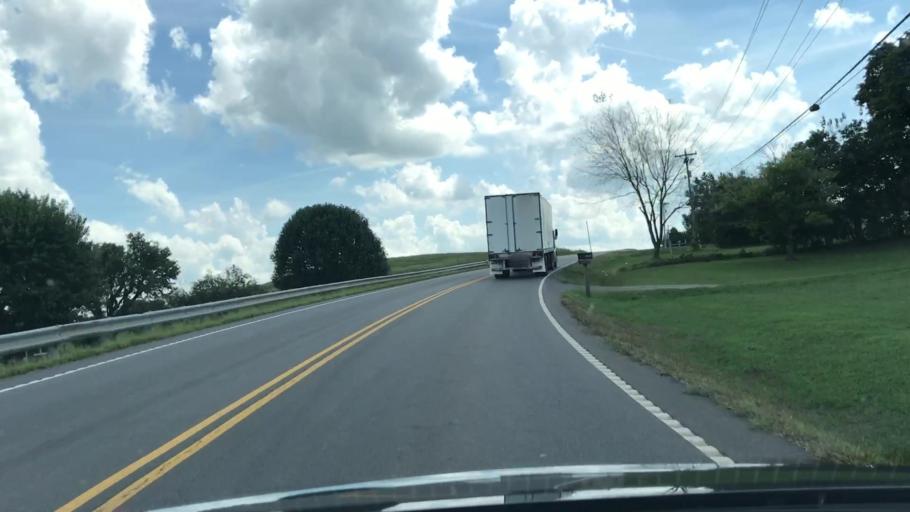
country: US
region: Tennessee
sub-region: Robertson County
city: Cross Plains
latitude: 36.5345
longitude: -86.6524
